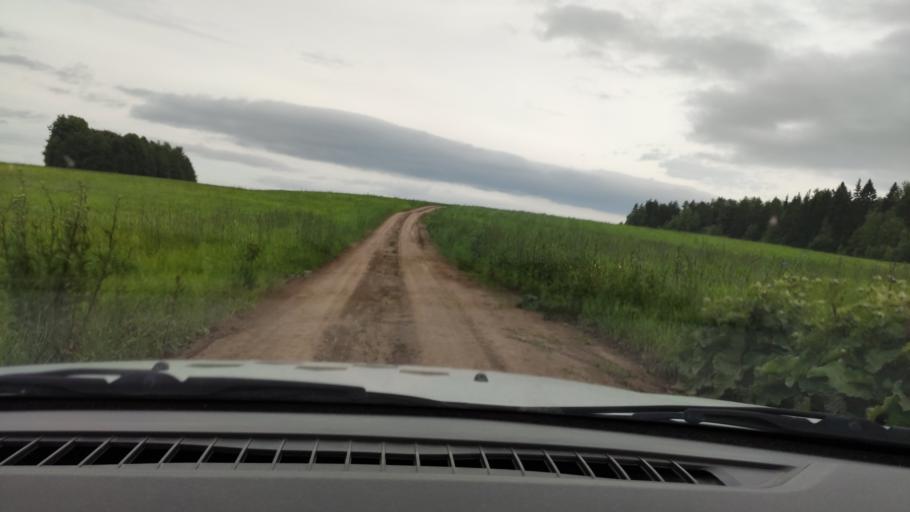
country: RU
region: Perm
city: Orda
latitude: 57.2996
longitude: 56.5907
